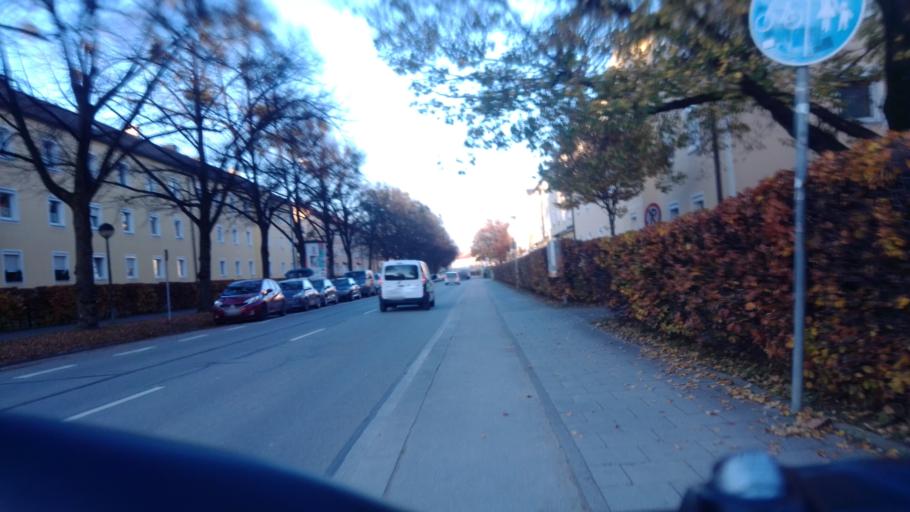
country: DE
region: Bavaria
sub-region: Upper Bavaria
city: Pullach im Isartal
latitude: 48.1041
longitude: 11.5310
